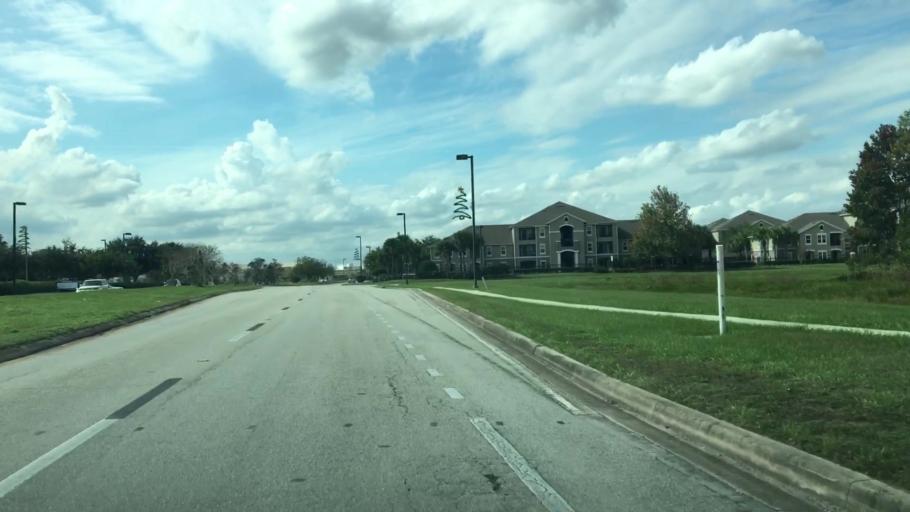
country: US
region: Florida
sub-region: Orange County
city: Conway
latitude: 28.4662
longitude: -81.2989
